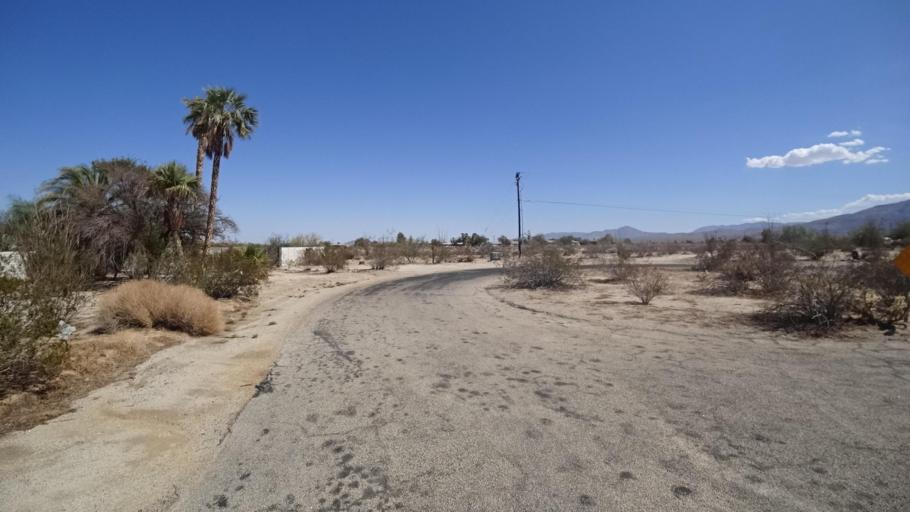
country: US
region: California
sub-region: San Diego County
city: Borrego Springs
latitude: 33.2352
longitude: -116.3779
